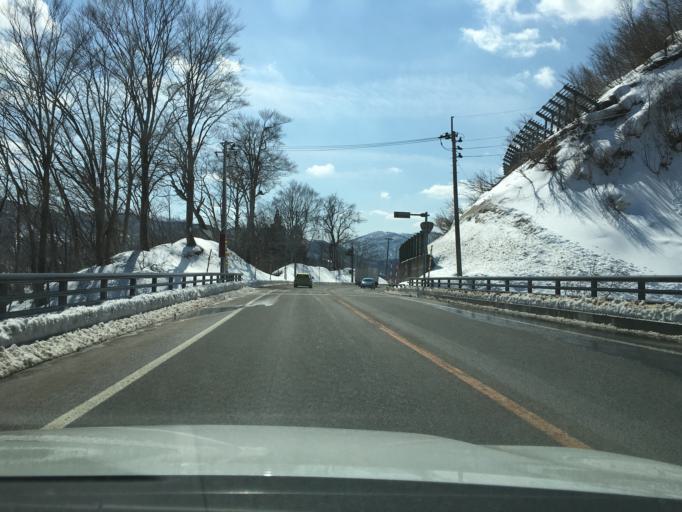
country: JP
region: Yamagata
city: Tsuruoka
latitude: 38.5804
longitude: 139.9367
